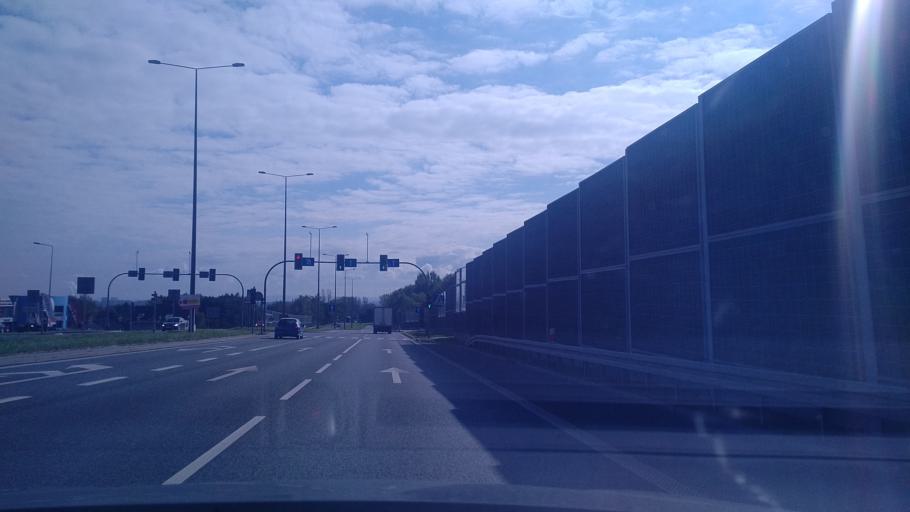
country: PL
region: Lesser Poland Voivodeship
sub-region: Powiat krakowski
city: Modlniczka
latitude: 50.1132
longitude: 19.8723
